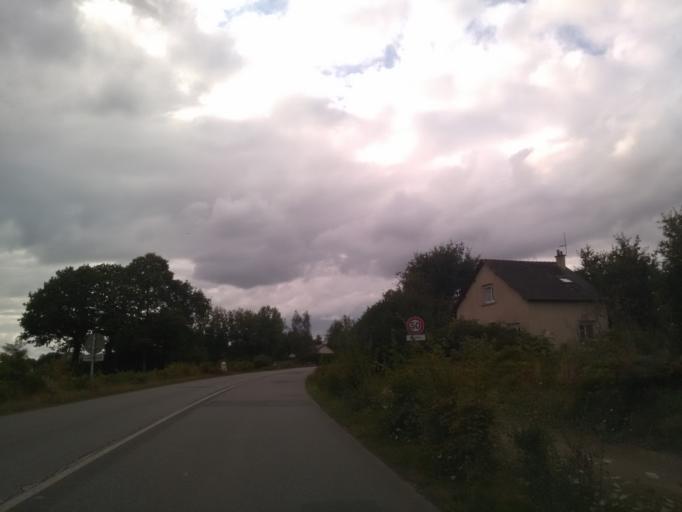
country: FR
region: Brittany
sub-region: Departement d'Ille-et-Vilaine
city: Vignoc
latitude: 48.2514
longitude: -1.7764
